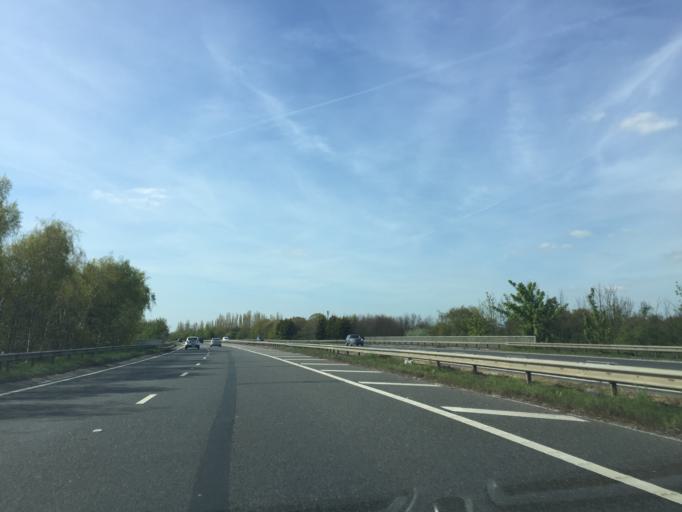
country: GB
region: England
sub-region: Kent
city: Swanley
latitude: 51.4055
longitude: 0.1540
